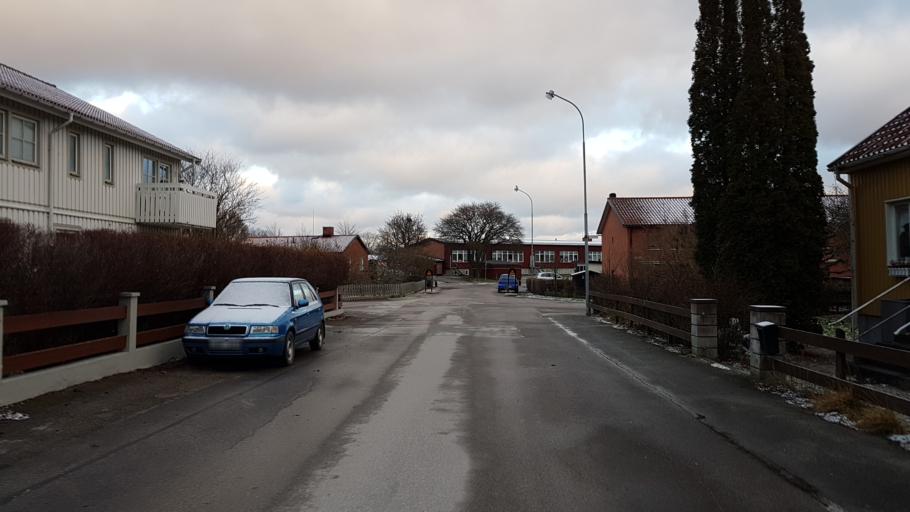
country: SE
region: Gotland
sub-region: Gotland
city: Visby
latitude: 57.6191
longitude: 18.2875
